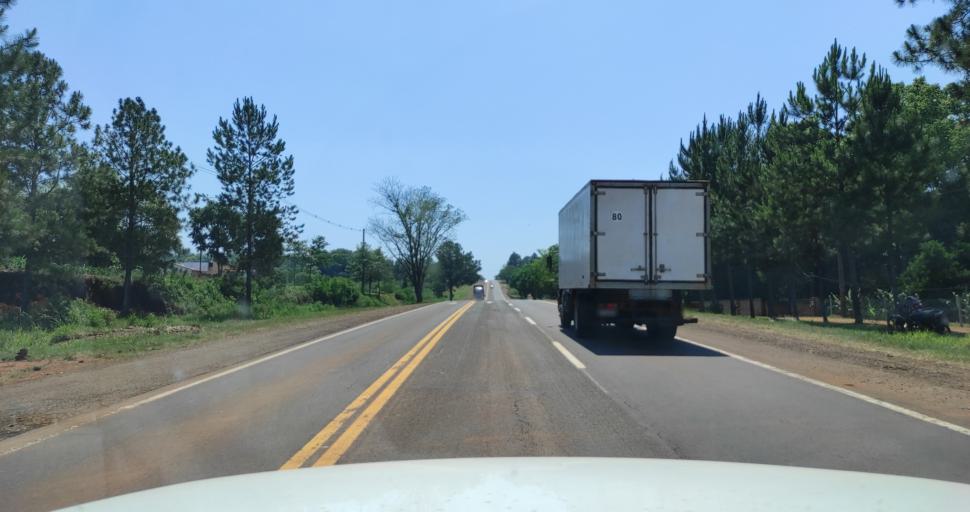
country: AR
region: Misiones
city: Santo Pipo
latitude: -27.1503
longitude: -55.4166
